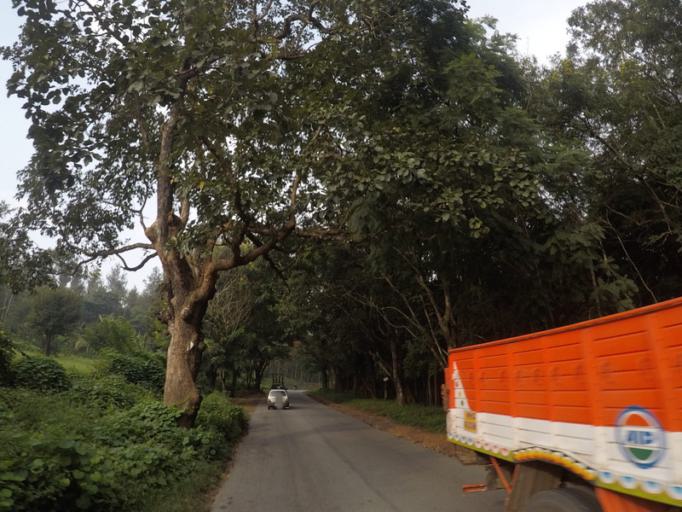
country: IN
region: Karnataka
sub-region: Chikmagalur
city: Chikmagalur
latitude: 13.2764
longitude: 75.7288
